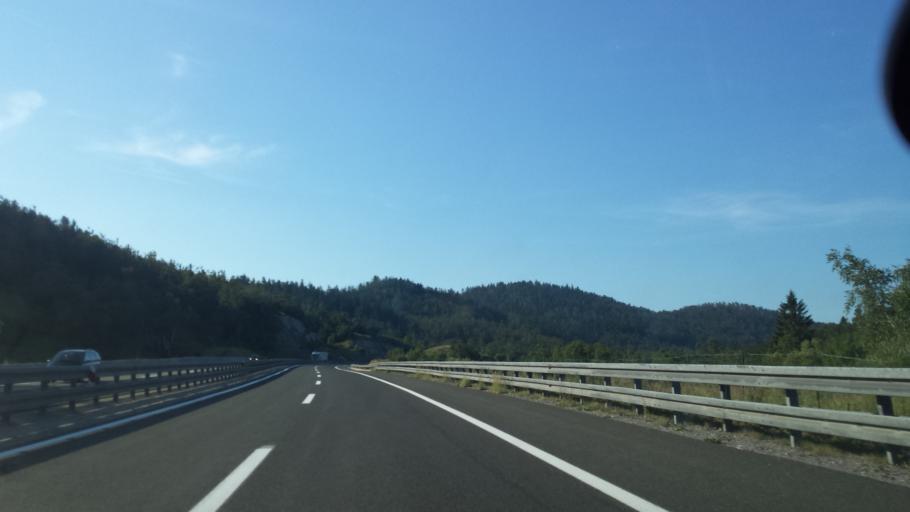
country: HR
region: Primorsko-Goranska
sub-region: Grad Delnice
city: Delnice
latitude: 45.3300
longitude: 14.7391
